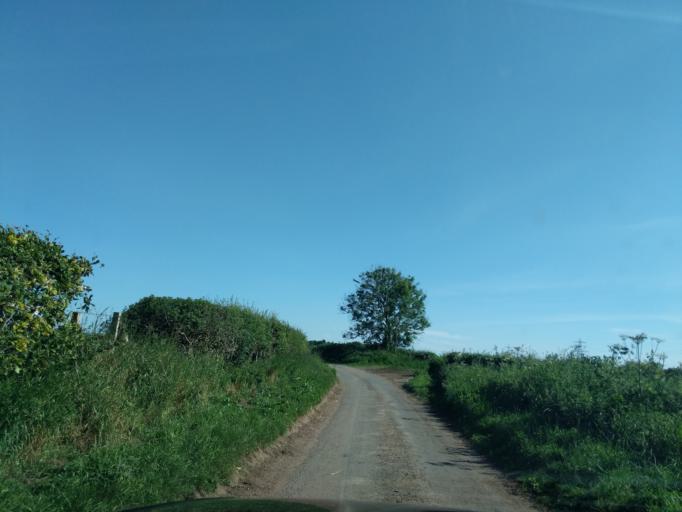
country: GB
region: Scotland
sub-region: East Lothian
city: Ormiston
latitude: 55.8818
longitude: -2.9347
